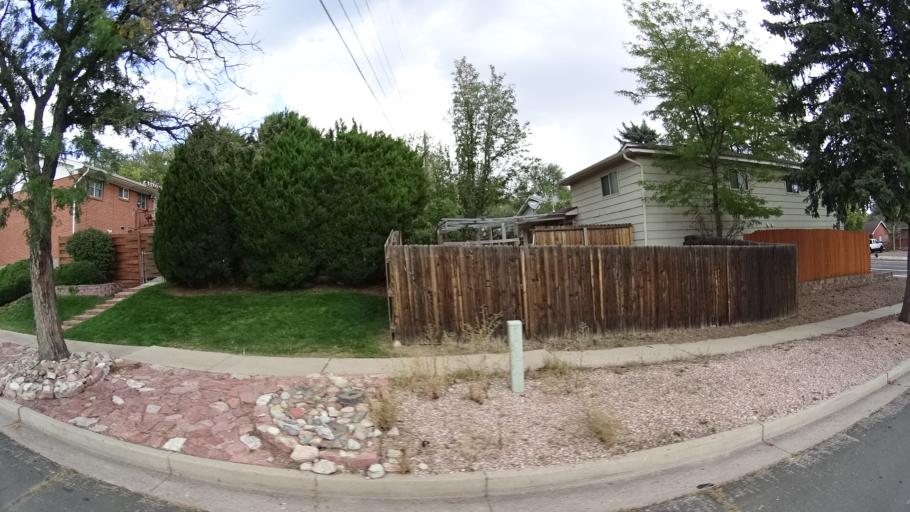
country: US
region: Colorado
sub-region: El Paso County
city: Colorado Springs
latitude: 38.8520
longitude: -104.7660
